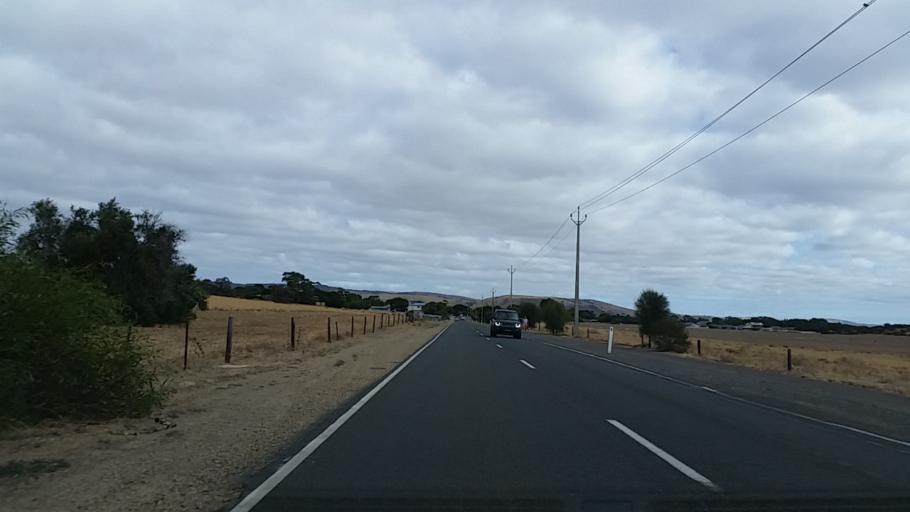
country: AU
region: South Australia
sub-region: Yankalilla
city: Normanville
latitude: -35.4380
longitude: 138.3195
